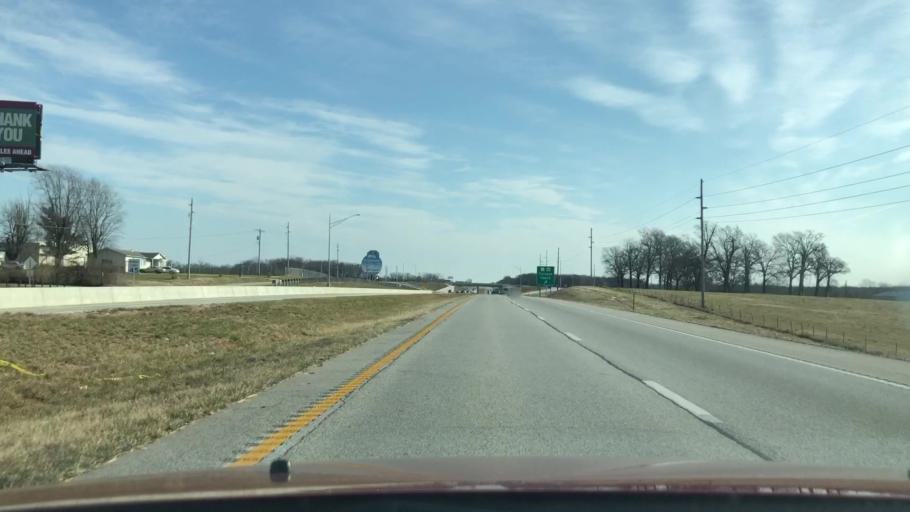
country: US
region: Missouri
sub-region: Christian County
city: Ozark
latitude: 37.1204
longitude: -93.1952
